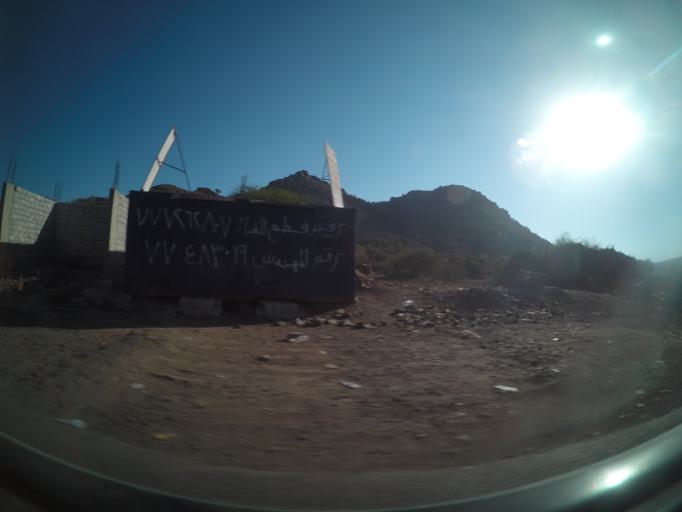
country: YE
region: Ad Dali'
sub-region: Ad Dhale'e
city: Dhalie
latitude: 13.6729
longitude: 44.7647
